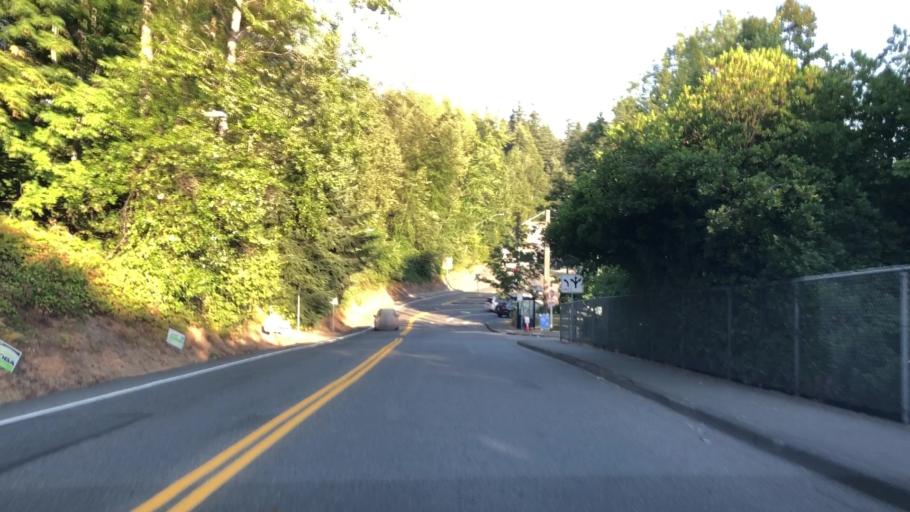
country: US
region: Washington
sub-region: King County
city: Bothell
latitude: 47.7598
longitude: -122.2006
